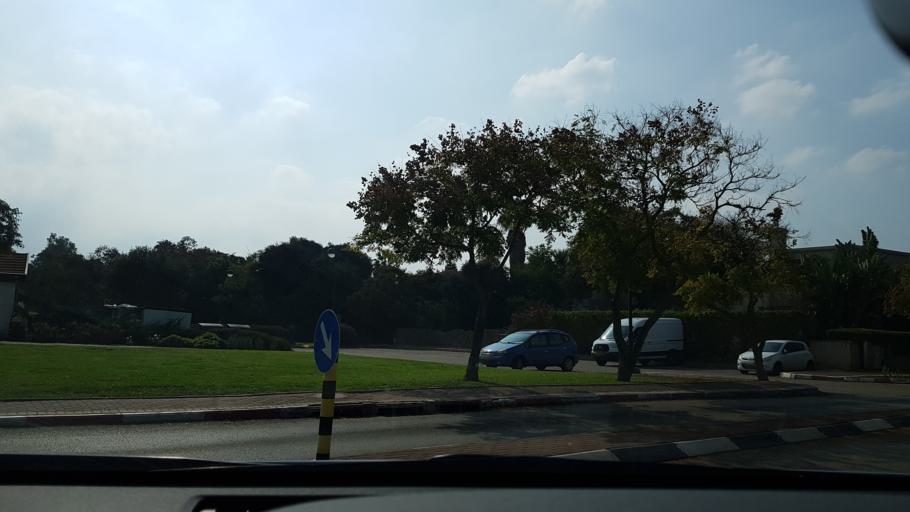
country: IL
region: Central District
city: Mazkeret Batya
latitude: 31.8704
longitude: 34.8275
